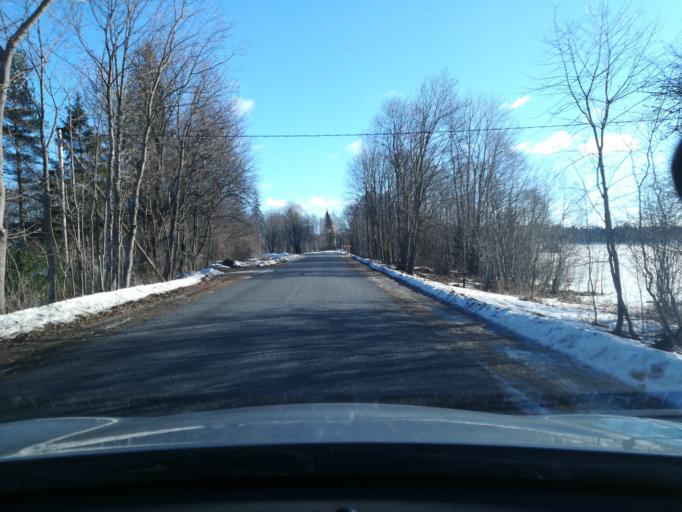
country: EE
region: Raplamaa
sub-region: Kohila vald
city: Kohila
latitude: 59.2326
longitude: 24.7692
